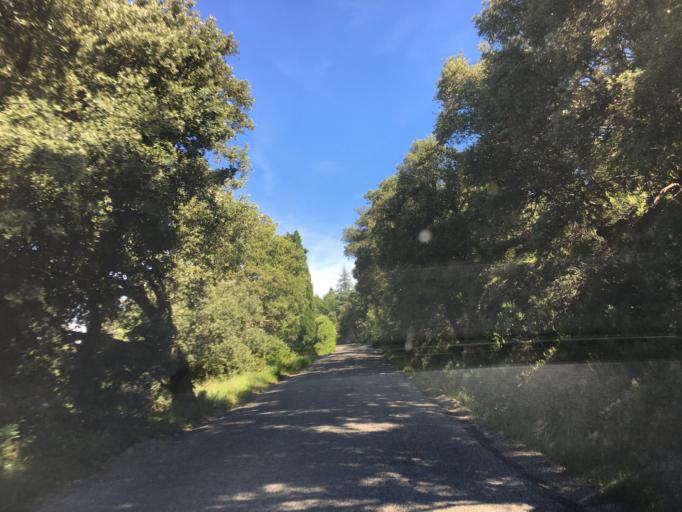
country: FR
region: Rhone-Alpes
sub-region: Departement de la Drome
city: Saint-Restitut
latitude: 44.3231
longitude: 4.7879
